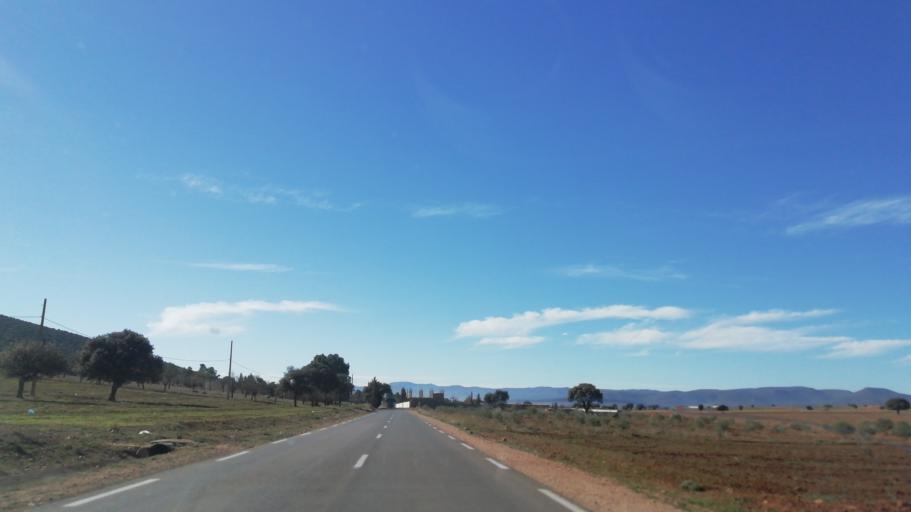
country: DZ
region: Tlemcen
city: Sebdou
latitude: 34.6868
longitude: -1.2479
